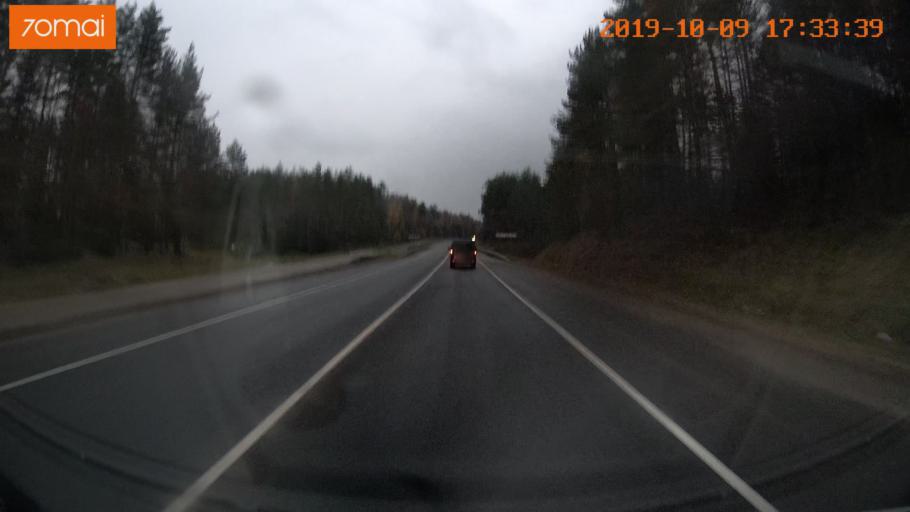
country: RU
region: Ivanovo
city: Bogorodskoye
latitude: 57.1153
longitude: 41.0184
